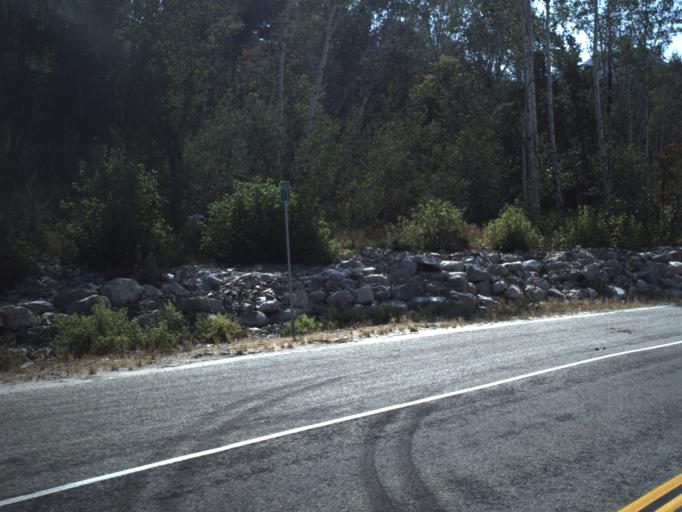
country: US
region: Utah
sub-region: Morgan County
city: Mountain Green
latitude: 41.2106
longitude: -111.8468
